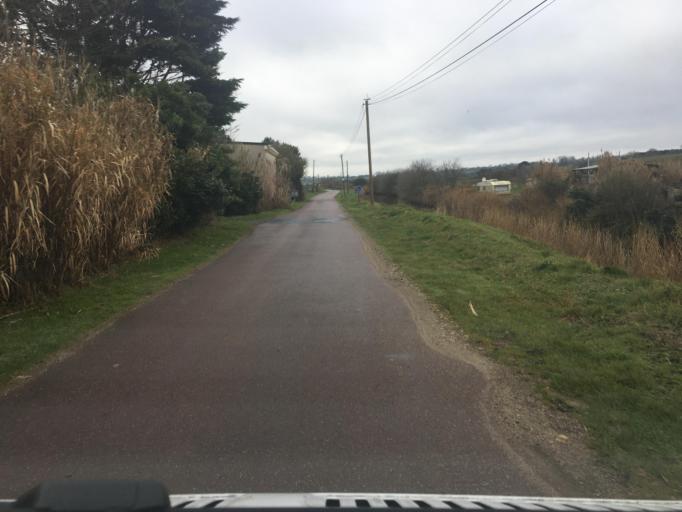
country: FR
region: Lower Normandy
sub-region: Departement du Calvados
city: Grandcamp-Maisy
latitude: 49.3930
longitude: -1.0193
